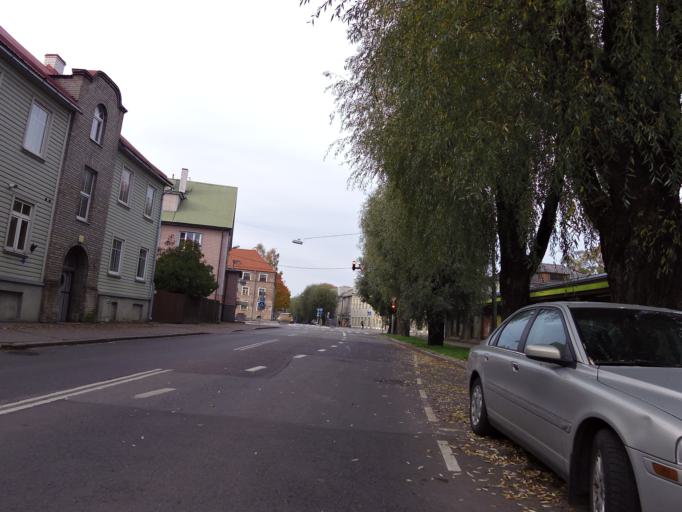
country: EE
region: Harju
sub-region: Tallinna linn
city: Tallinn
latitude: 59.4354
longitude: 24.7210
